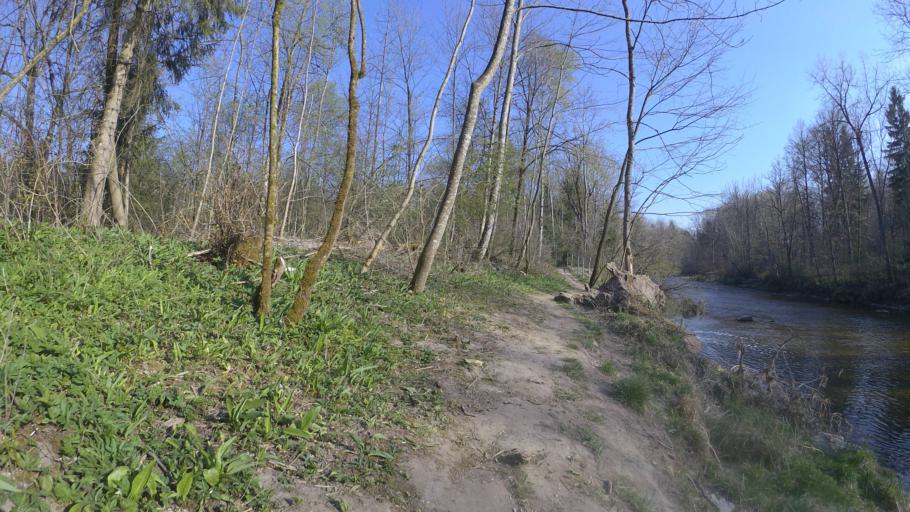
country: DE
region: Bavaria
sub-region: Upper Bavaria
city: Traunreut
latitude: 47.9514
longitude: 12.5860
